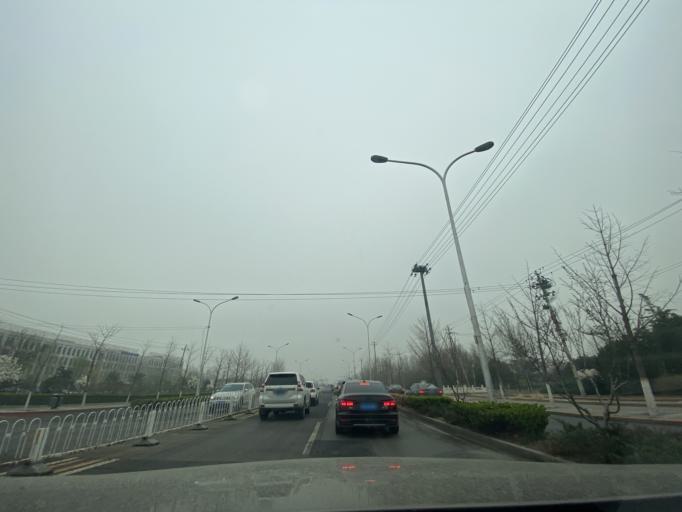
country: CN
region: Beijing
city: Sijiqing
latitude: 39.9719
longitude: 116.2484
